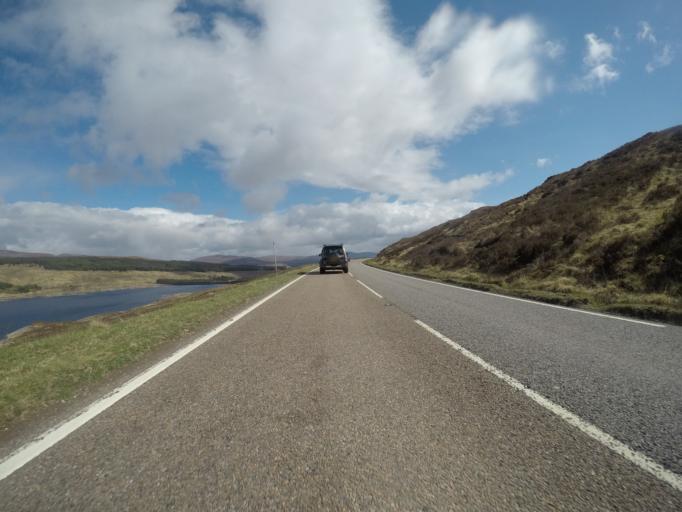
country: GB
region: Scotland
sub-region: Highland
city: Spean Bridge
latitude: 57.1190
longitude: -4.9786
